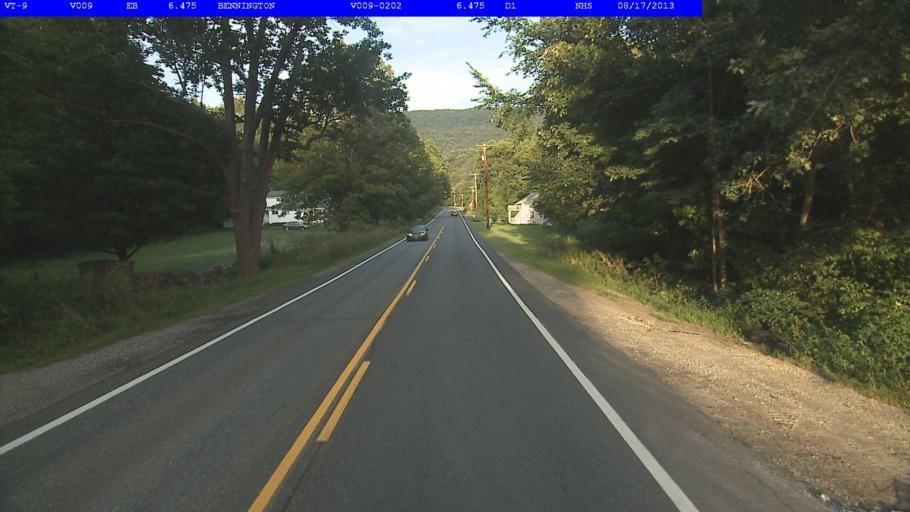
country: US
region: Vermont
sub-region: Bennington County
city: Bennington
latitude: 42.8832
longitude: -73.1575
